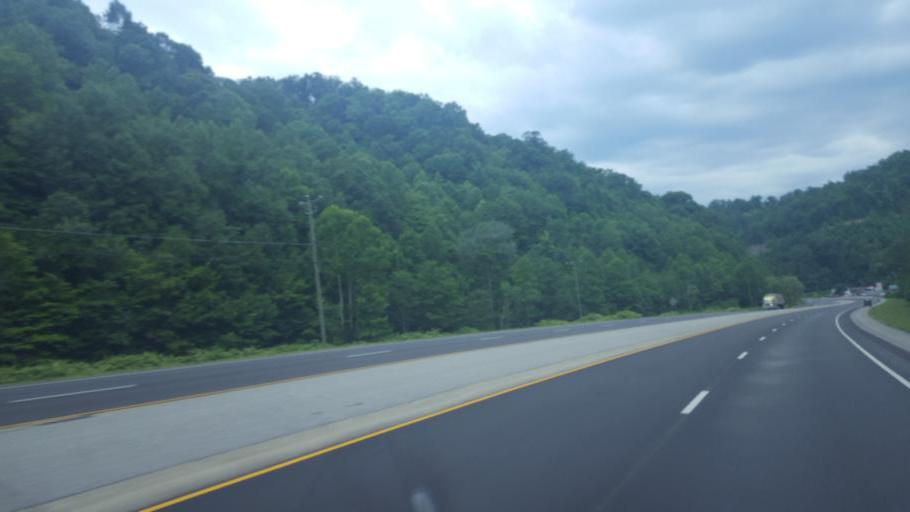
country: US
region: Kentucky
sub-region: Letcher County
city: Jenkins
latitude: 37.2818
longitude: -82.5673
